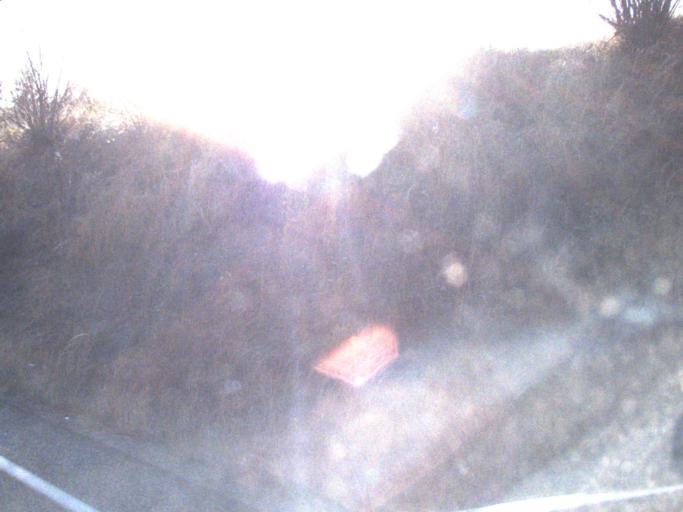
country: CA
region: British Columbia
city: Rossland
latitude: 48.8817
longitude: -117.8335
